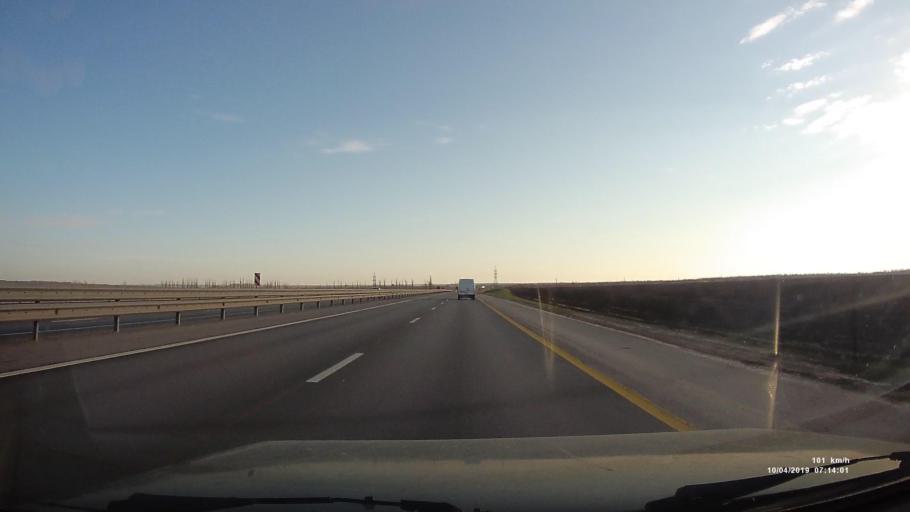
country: RU
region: Rostov
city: Ayutinskiy
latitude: 47.7441
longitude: 40.1327
